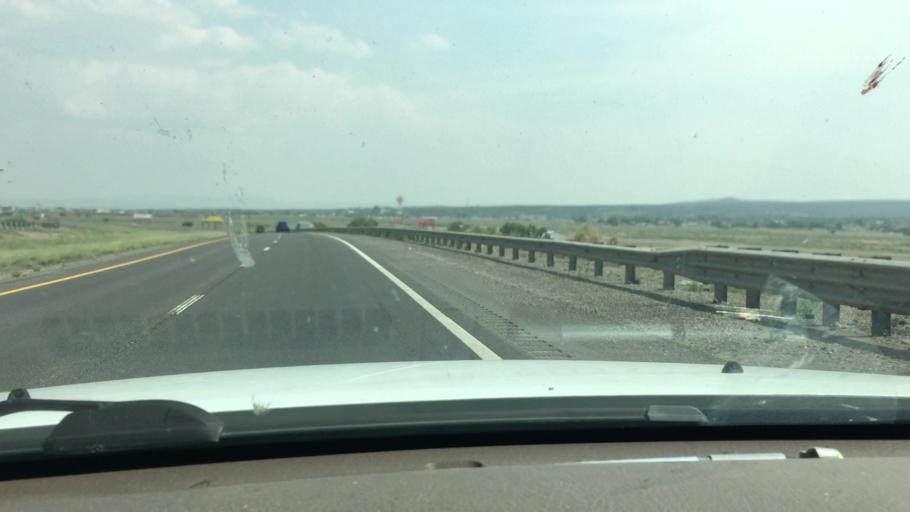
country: US
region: New Mexico
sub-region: Cibola County
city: Milan
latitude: 35.1691
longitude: -107.8993
